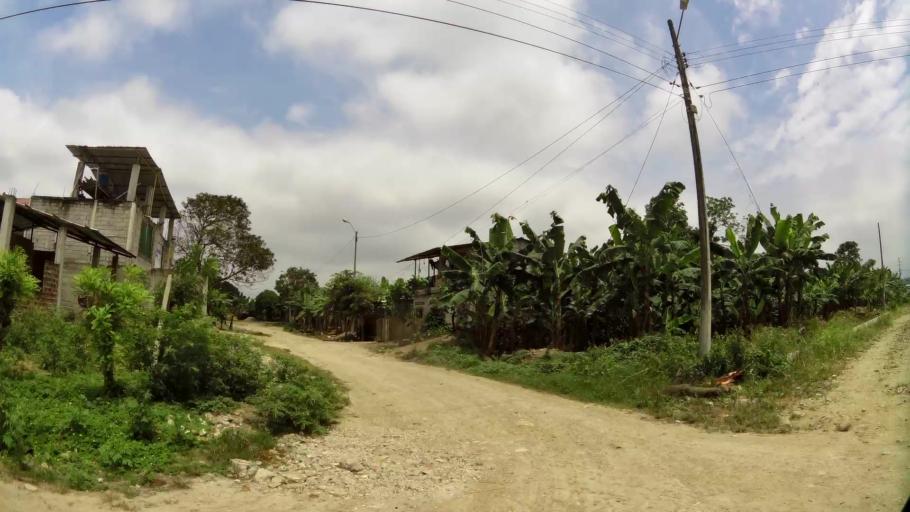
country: EC
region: El Oro
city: Pasaje
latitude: -3.2389
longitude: -79.8257
